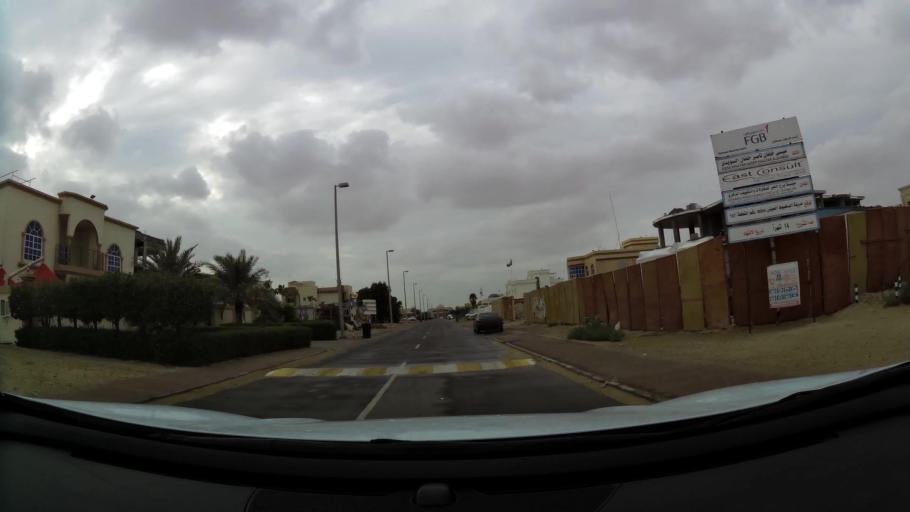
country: AE
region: Abu Dhabi
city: Abu Dhabi
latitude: 24.3523
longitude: 54.6315
